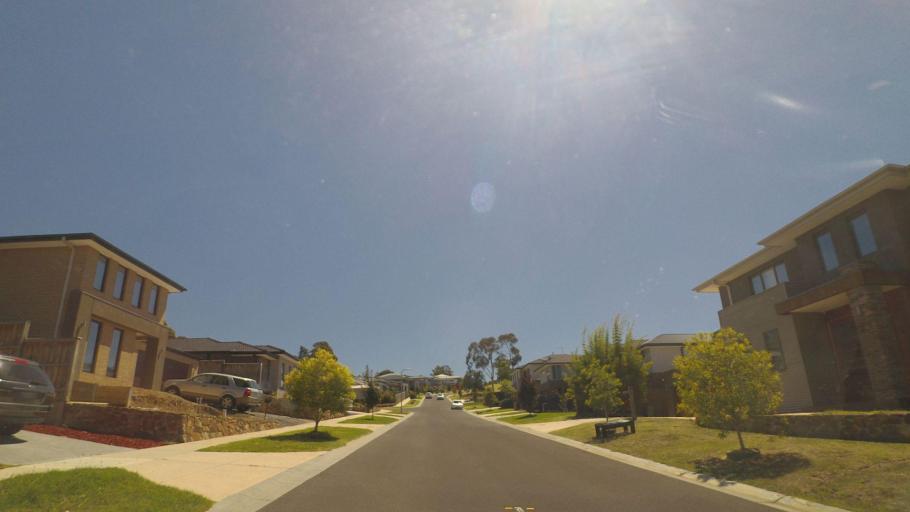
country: AU
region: Victoria
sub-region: Yarra Ranges
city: Lilydale
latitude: -37.7497
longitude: 145.3309
